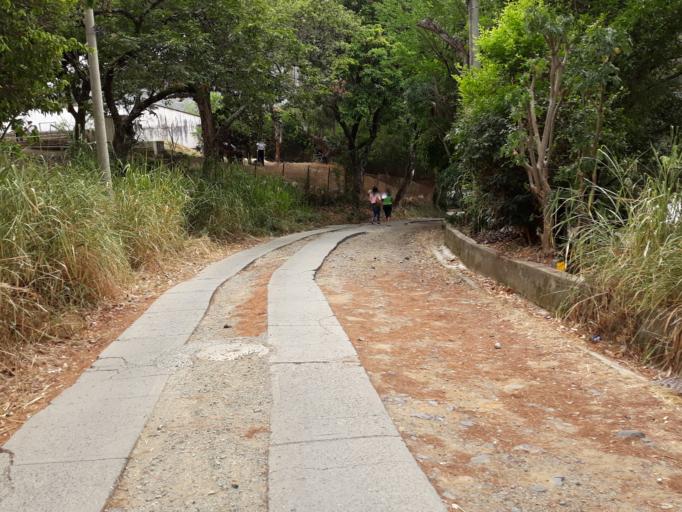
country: CO
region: Valle del Cauca
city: Cali
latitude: 3.4620
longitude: -76.5603
